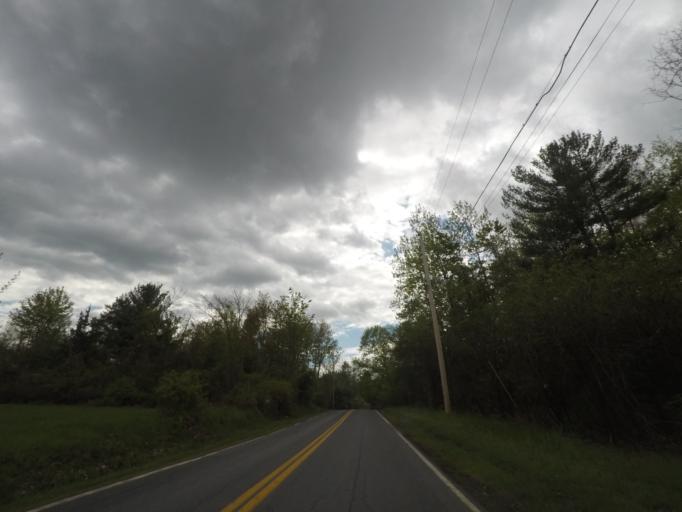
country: US
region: New York
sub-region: Albany County
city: Voorheesville
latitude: 42.6871
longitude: -73.9285
